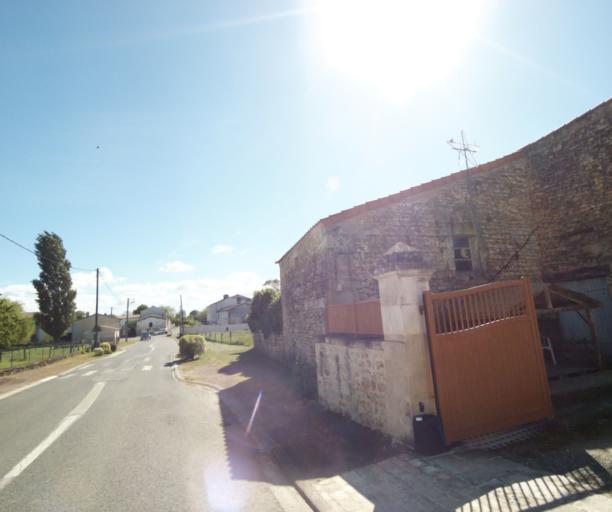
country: FR
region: Poitou-Charentes
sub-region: Departement de la Charente-Maritime
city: Bussac-sur-Charente
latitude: 45.8228
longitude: -0.6584
